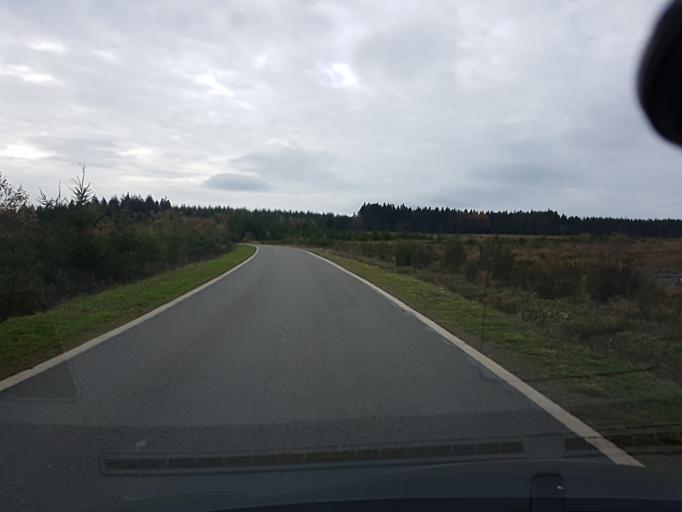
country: BE
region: Wallonia
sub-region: Province de Liege
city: Malmedy
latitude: 50.4716
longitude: 6.0377
